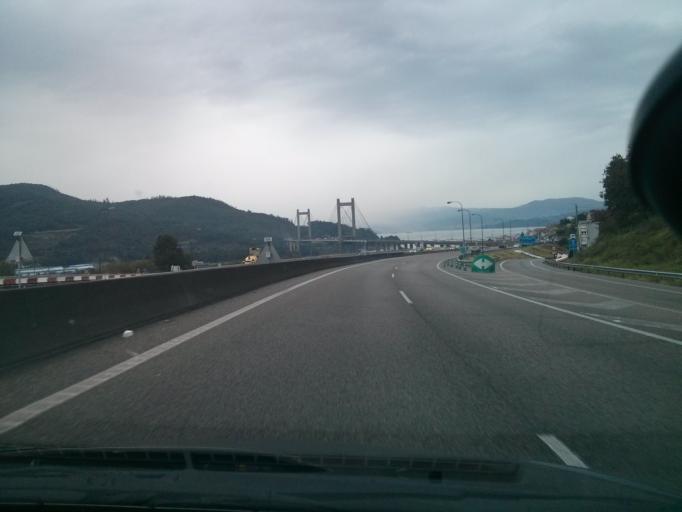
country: ES
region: Galicia
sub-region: Provincia de Pontevedra
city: Redondela
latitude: 42.2769
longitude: -8.6656
